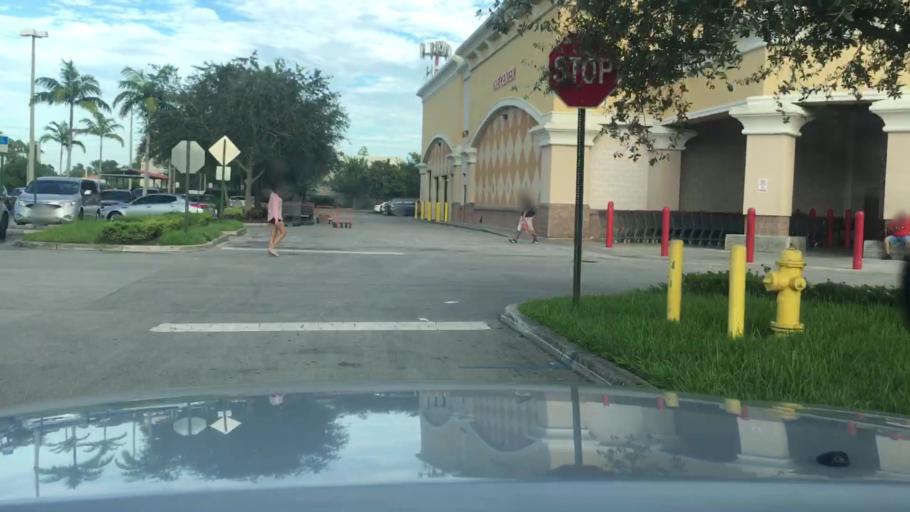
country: US
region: Florida
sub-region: Miami-Dade County
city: Three Lakes
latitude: 25.6542
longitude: -80.4129
